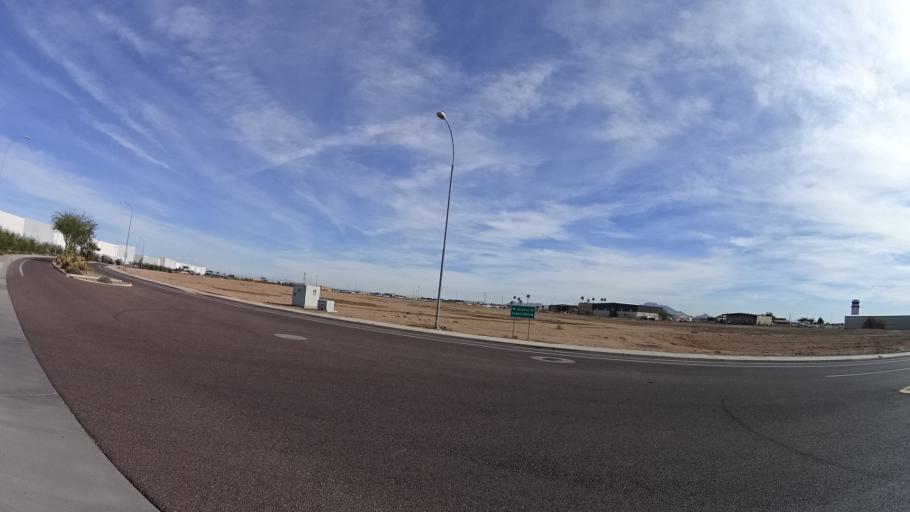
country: US
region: Arizona
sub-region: Maricopa County
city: Chandler
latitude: 33.2752
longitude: -111.8151
